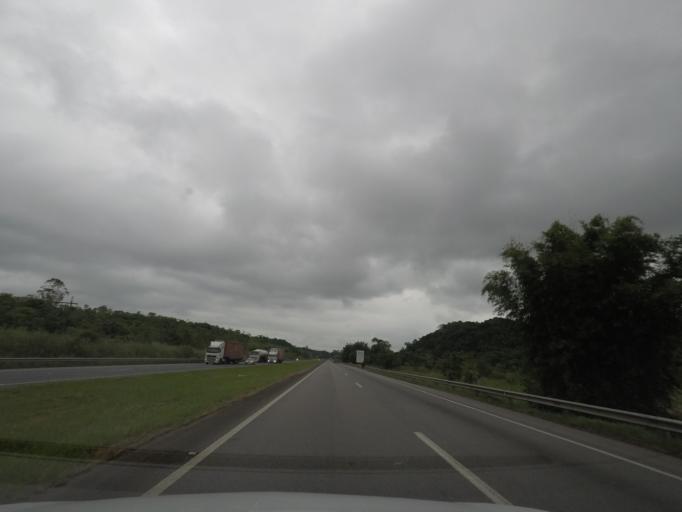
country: BR
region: Sao Paulo
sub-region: Registro
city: Registro
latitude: -24.4124
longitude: -47.7551
